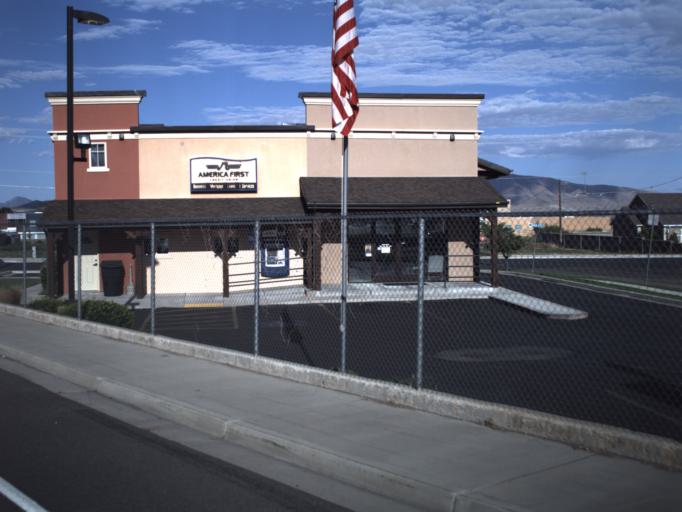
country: US
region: Utah
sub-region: Utah County
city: Salem
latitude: 40.0574
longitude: -111.6726
